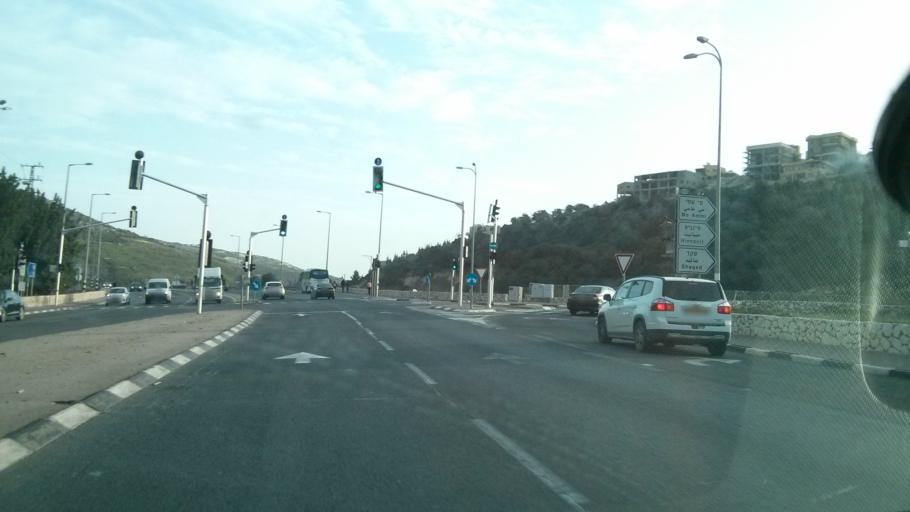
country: IL
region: Haifa
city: Umm el Fahm
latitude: 32.5140
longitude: 35.1195
